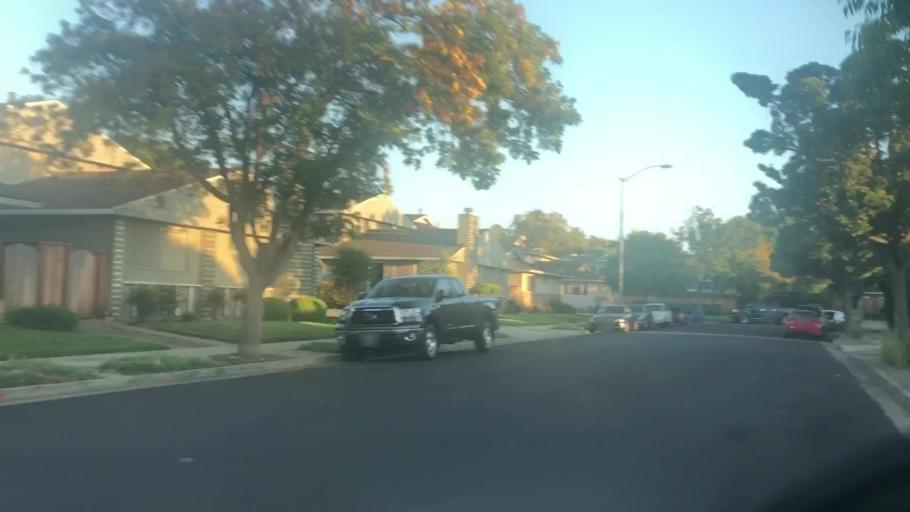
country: US
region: California
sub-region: Santa Clara County
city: Campbell
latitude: 37.2849
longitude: -121.9814
